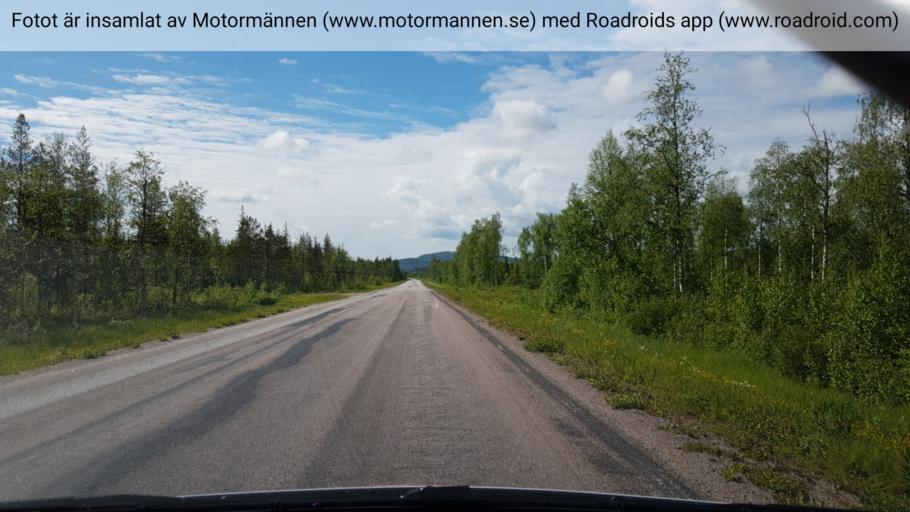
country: FI
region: Lapland
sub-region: Torniolaakso
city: Pello
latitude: 66.7078
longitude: 23.8533
